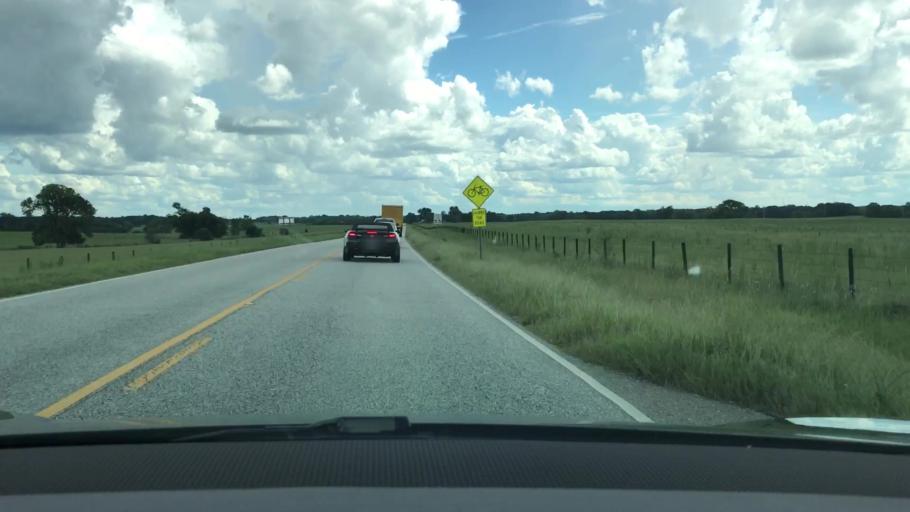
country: US
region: Alabama
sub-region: Montgomery County
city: Pike Road
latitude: 32.2724
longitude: -86.0998
